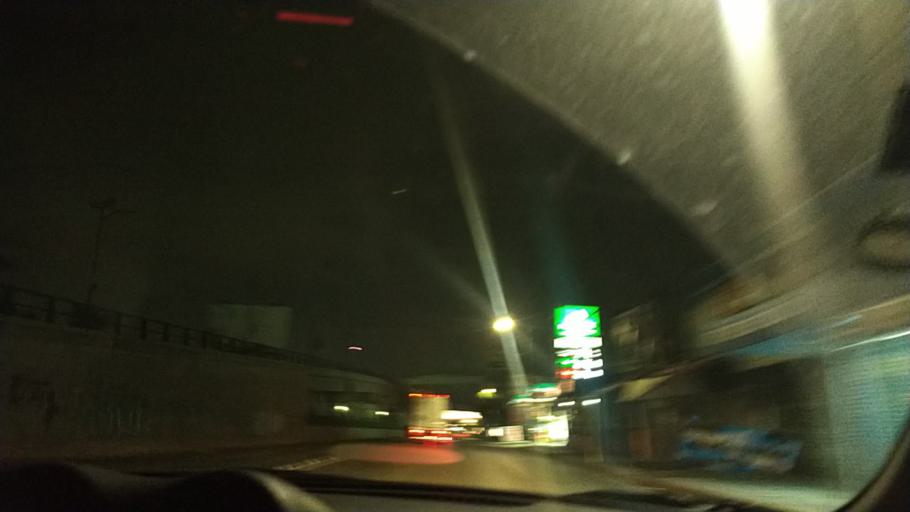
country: MX
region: Mexico
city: Ecatepec
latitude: 19.6256
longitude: -99.0780
